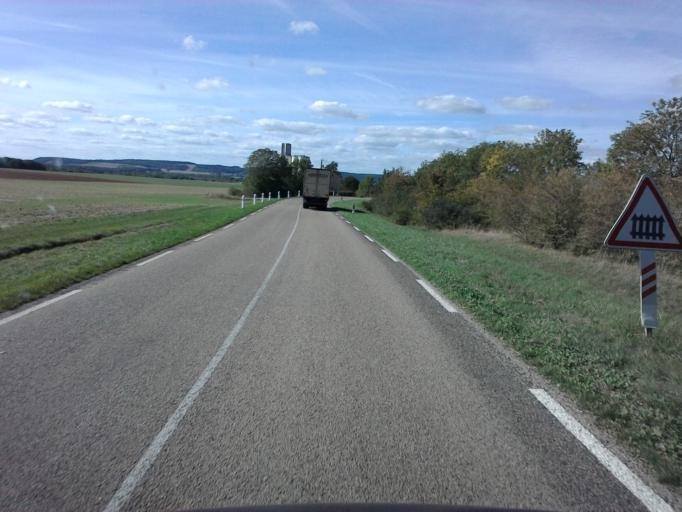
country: FR
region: Bourgogne
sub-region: Departement de la Cote-d'Or
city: Chatillon-sur-Seine
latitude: 47.9075
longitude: 4.6865
